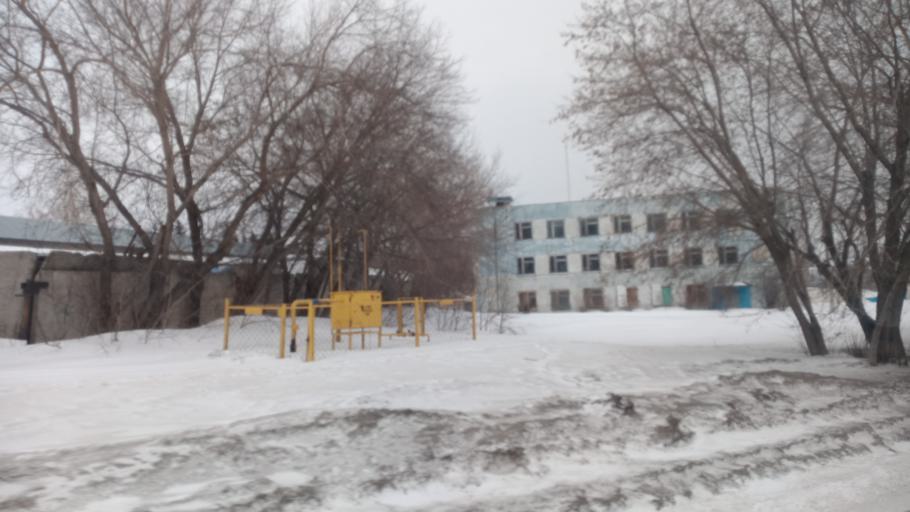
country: RU
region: Altai Krai
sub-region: Gorod Barnaulskiy
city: Barnaul
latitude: 53.3895
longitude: 83.6776
